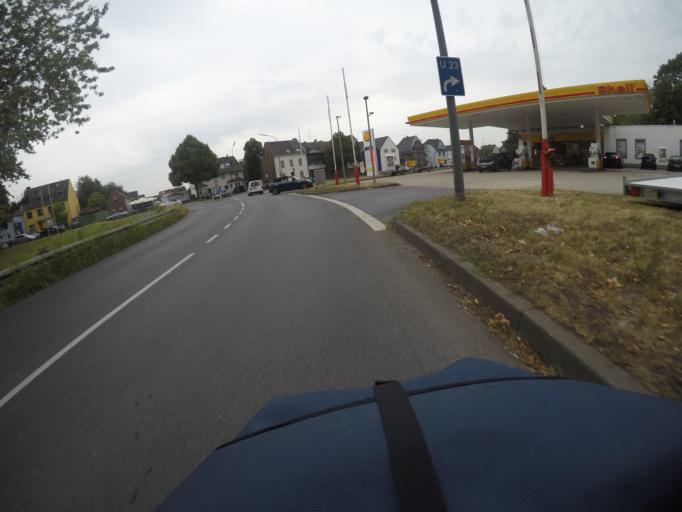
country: DE
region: North Rhine-Westphalia
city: Wesseling
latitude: 50.8525
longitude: 6.9762
